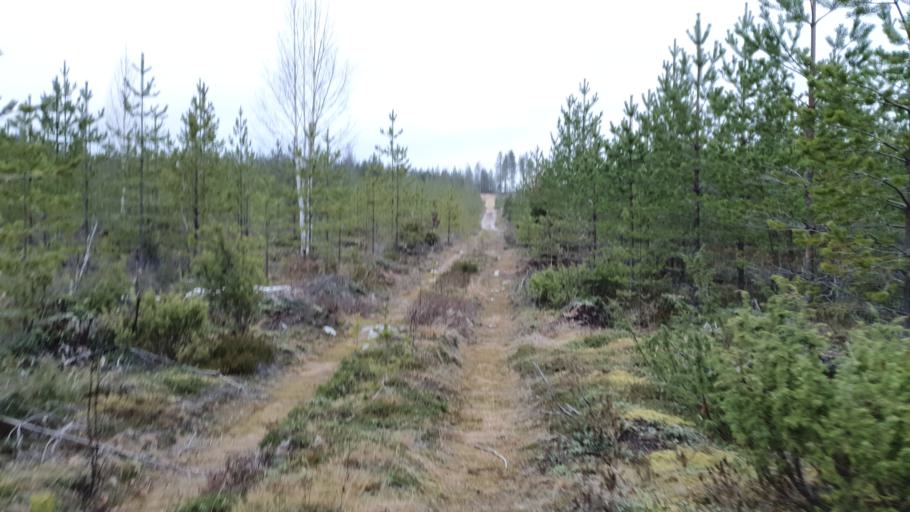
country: FI
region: Kainuu
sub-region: Kehys-Kainuu
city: Kuhmo
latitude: 64.1463
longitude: 29.4083
